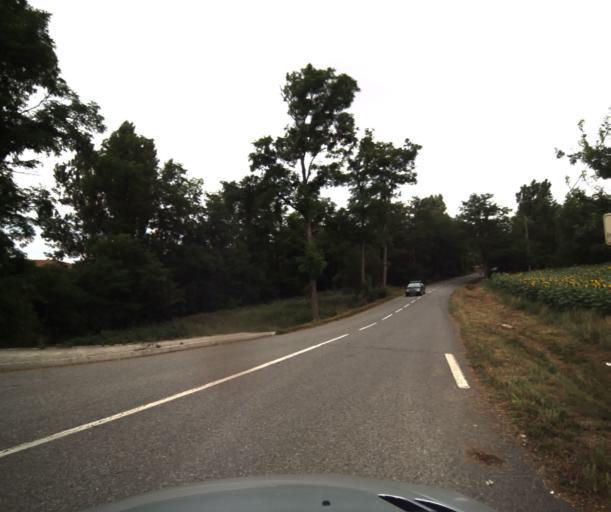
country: FR
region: Midi-Pyrenees
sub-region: Departement de la Haute-Garonne
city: Labarthe-sur-Leze
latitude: 43.4509
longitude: 1.4074
